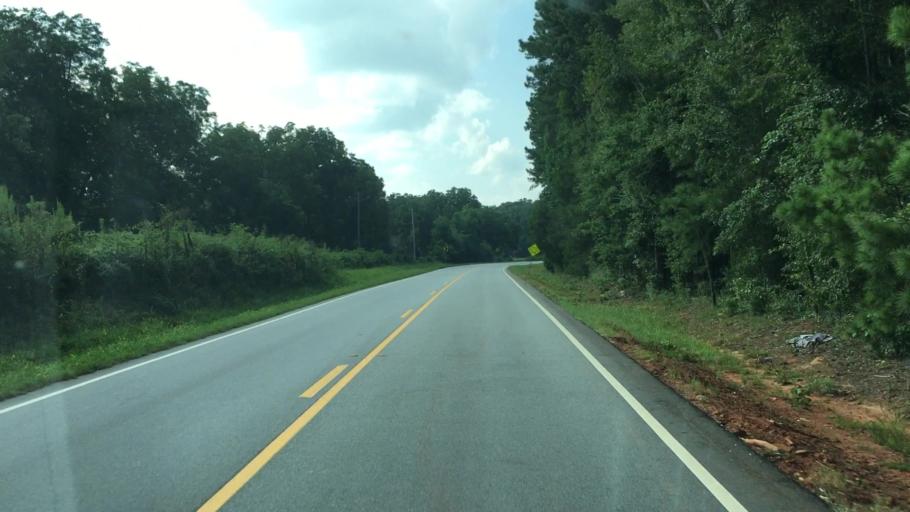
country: US
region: Georgia
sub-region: Jasper County
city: Monticello
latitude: 33.3947
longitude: -83.7580
